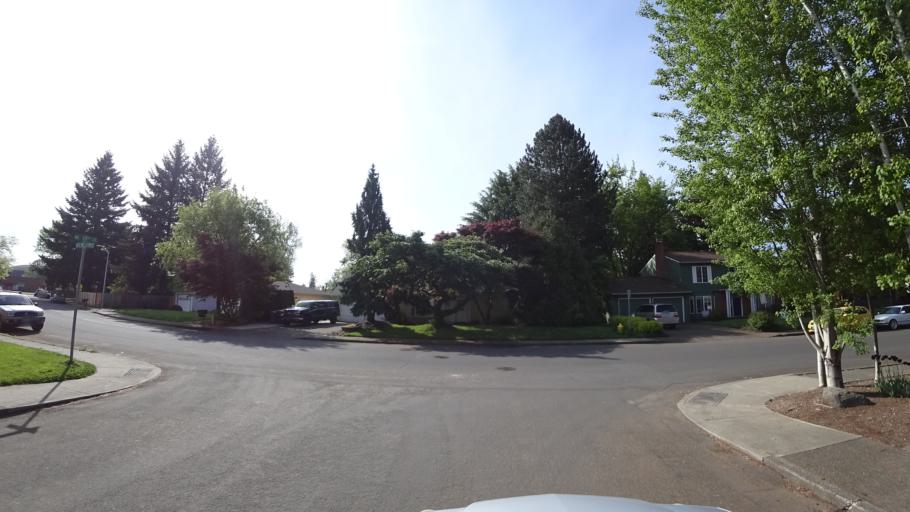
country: US
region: Oregon
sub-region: Washington County
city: Hillsboro
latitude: 45.5234
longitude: -122.9624
